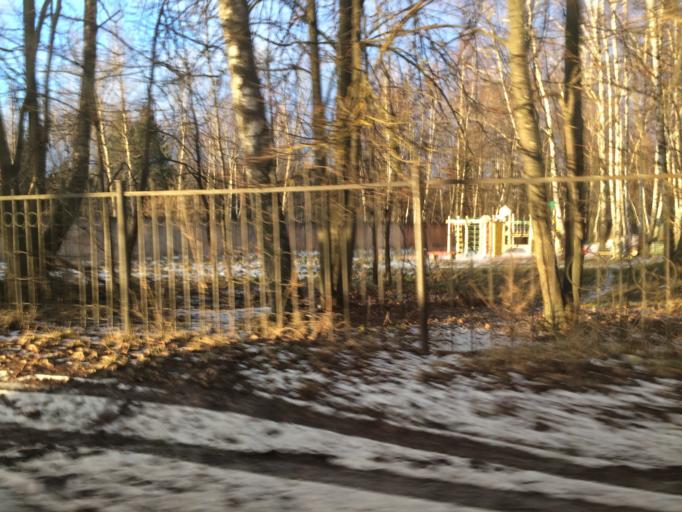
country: RU
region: Tula
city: Cherepet'
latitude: 54.1113
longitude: 36.3386
